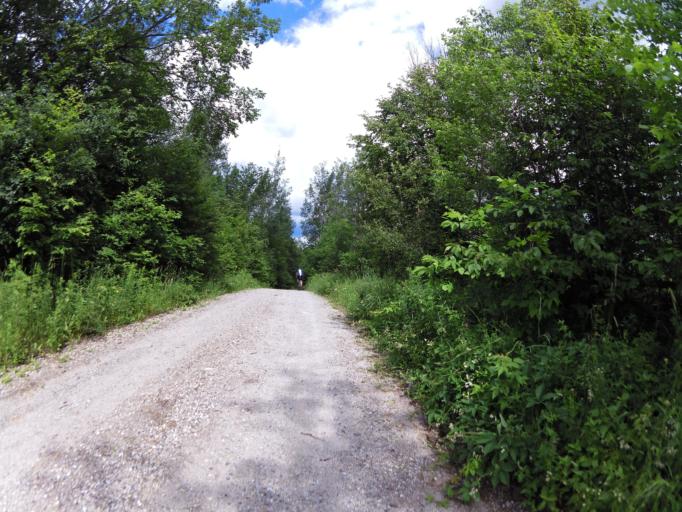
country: CA
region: Ontario
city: Perth
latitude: 45.0214
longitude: -76.5567
